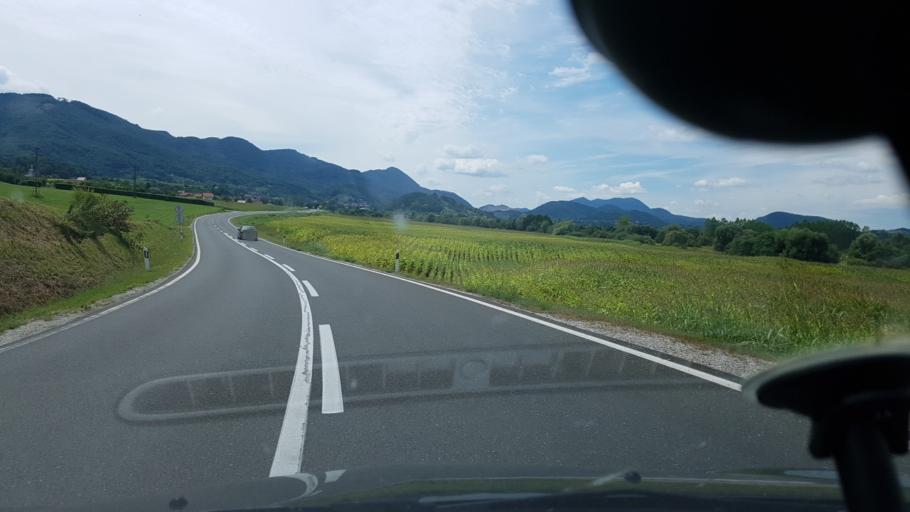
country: HR
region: Varazdinska
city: Ivanec
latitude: 46.2232
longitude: 16.0772
